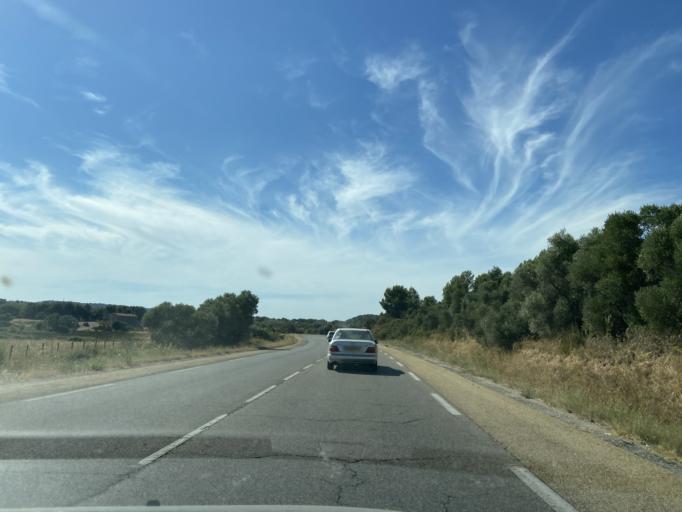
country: FR
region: Provence-Alpes-Cote d'Azur
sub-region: Departement des Bouches-du-Rhone
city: Saint-Chamas
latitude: 43.5306
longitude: 5.0537
